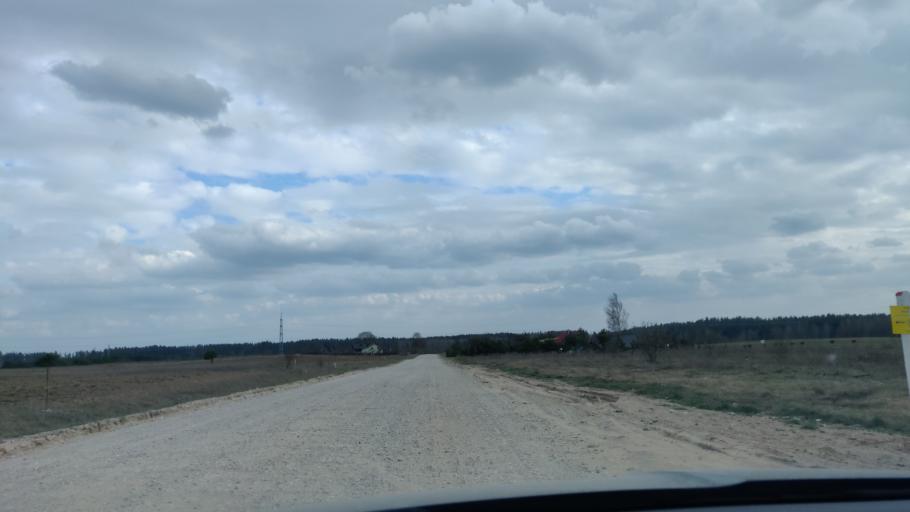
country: LT
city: Lentvaris
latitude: 54.6137
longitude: 25.0693
